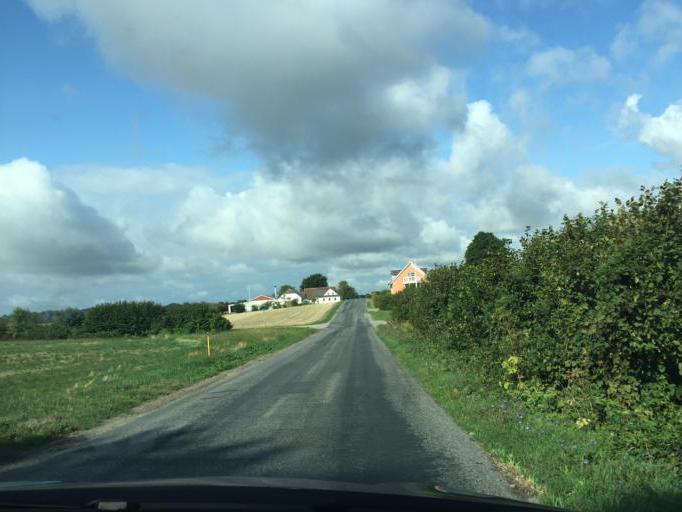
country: DK
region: South Denmark
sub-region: Faaborg-Midtfyn Kommune
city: Faaborg
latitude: 55.1961
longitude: 10.2673
